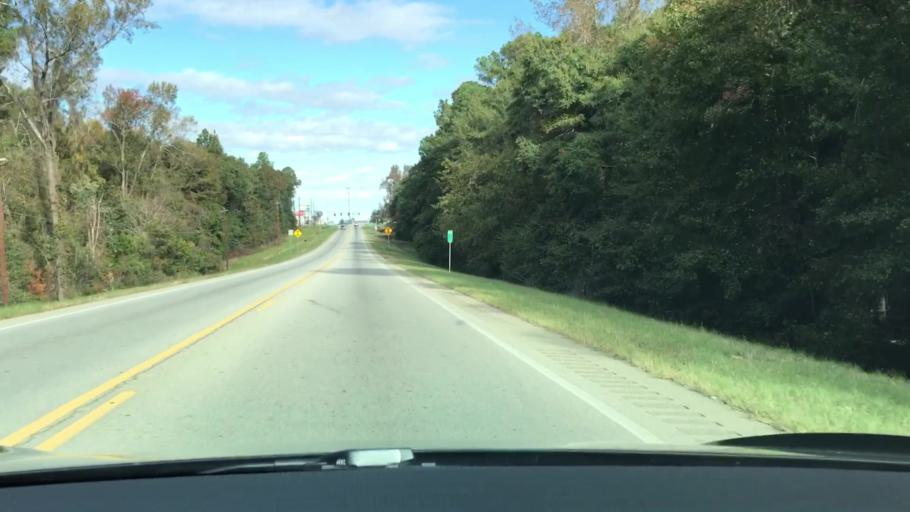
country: US
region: Georgia
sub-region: Jefferson County
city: Louisville
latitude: 33.0006
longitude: -82.3951
